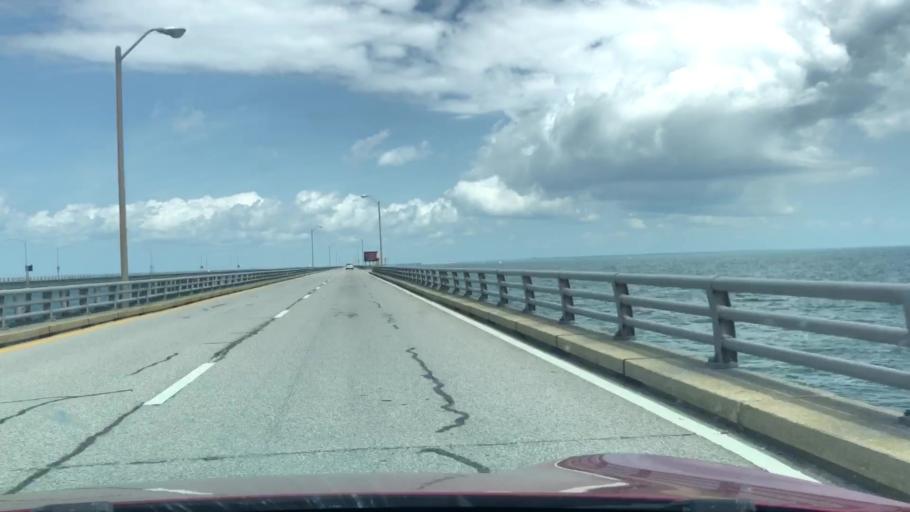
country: US
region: Virginia
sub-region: City of Virginia Beach
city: Virginia Beach
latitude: 36.9945
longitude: -76.1007
